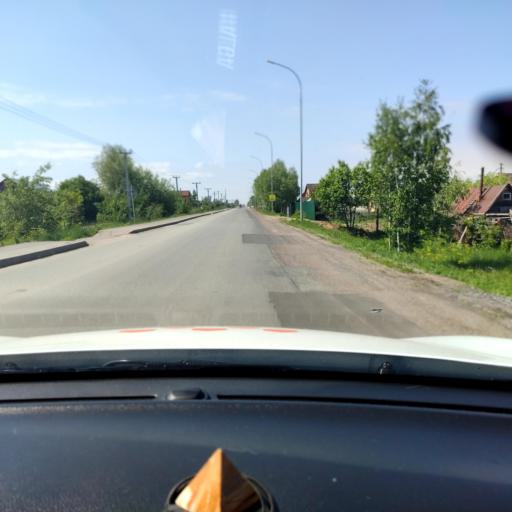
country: RU
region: Tatarstan
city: Stolbishchi
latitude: 55.6950
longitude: 49.1989
